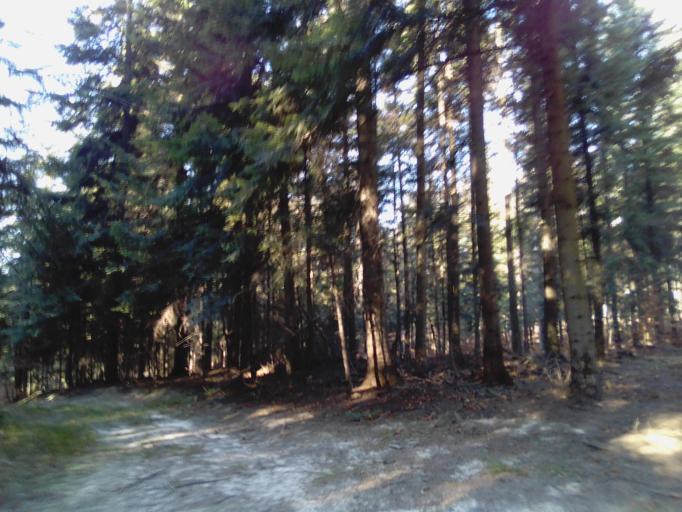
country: PL
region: Subcarpathian Voivodeship
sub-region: Powiat strzyzowski
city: Wisniowa
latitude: 49.8455
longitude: 21.6672
